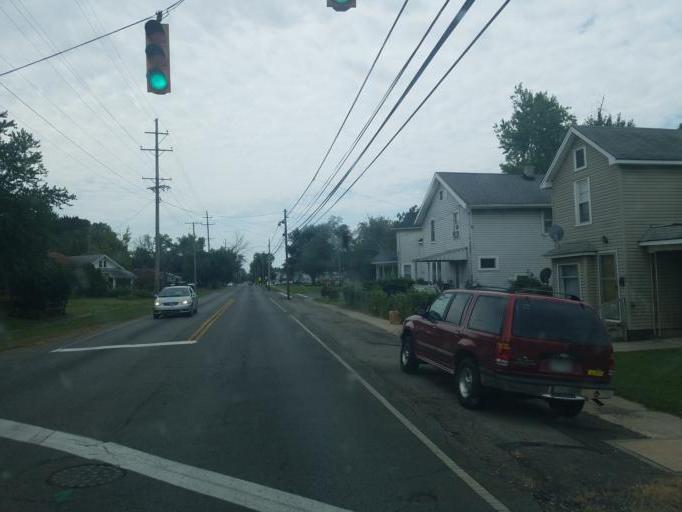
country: US
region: Ohio
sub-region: Marion County
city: Marion
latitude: 40.5731
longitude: -83.1455
